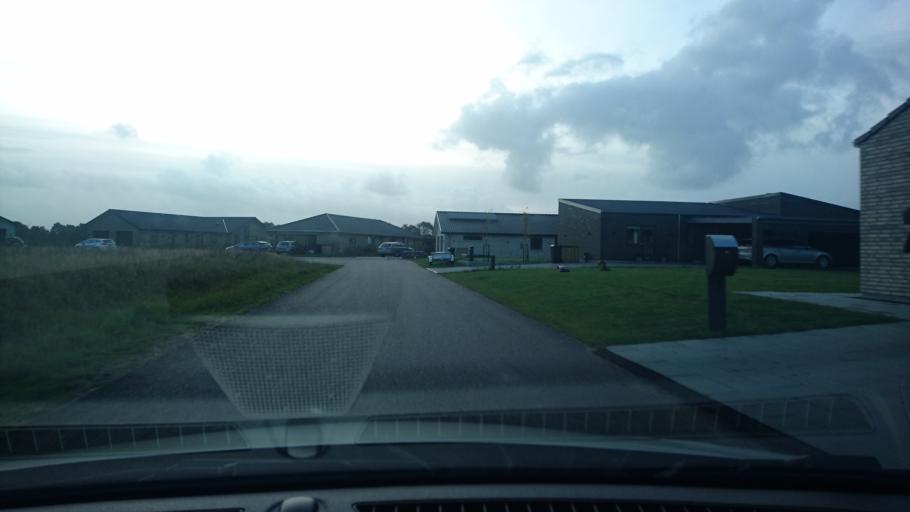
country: DK
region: South Denmark
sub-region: Billund Kommune
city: Billund
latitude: 55.7159
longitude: 9.1032
